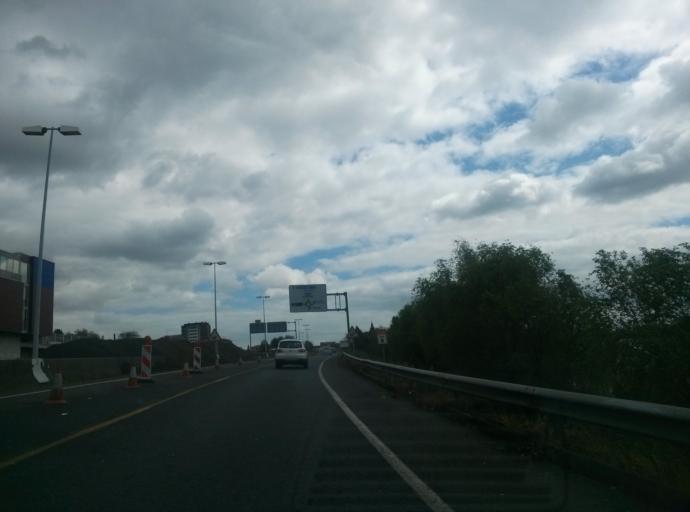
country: ES
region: Galicia
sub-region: Provincia da Coruna
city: Santiago de Compostela
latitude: 42.8642
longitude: -8.5609
